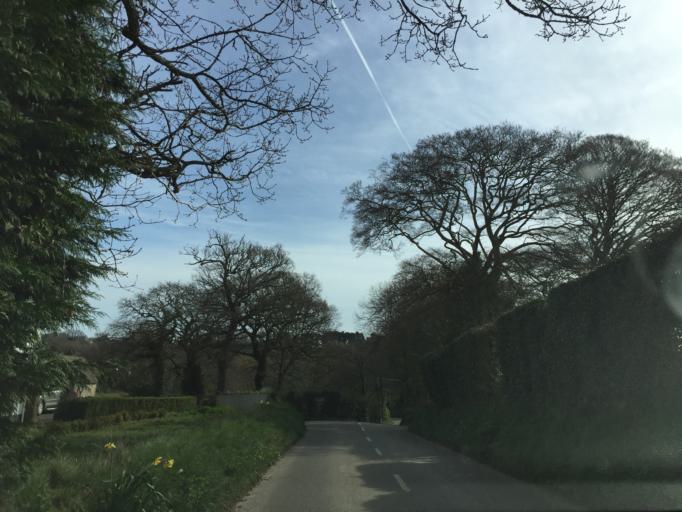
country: JE
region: St Helier
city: Saint Helier
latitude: 49.2235
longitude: -2.1370
